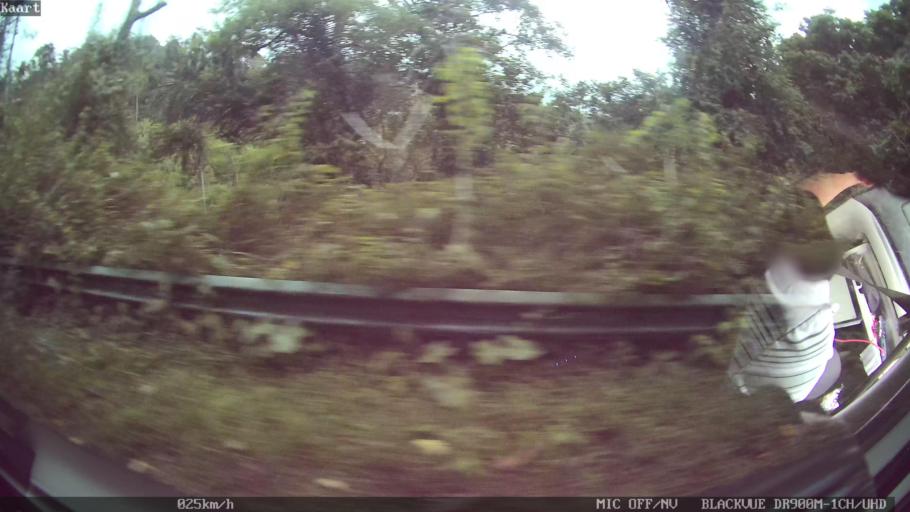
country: ID
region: Bali
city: Peneng
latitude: -8.3628
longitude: 115.2177
